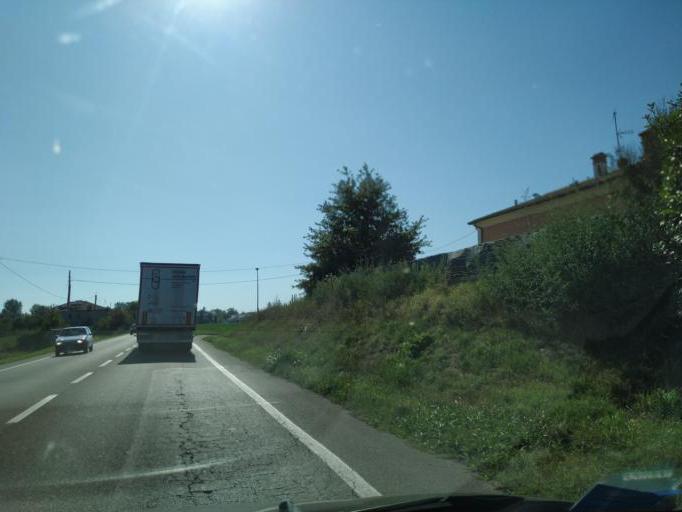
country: IT
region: Emilia-Romagna
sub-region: Provincia di Bologna
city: San Giovanni in Persiceto
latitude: 44.6485
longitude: 11.1611
